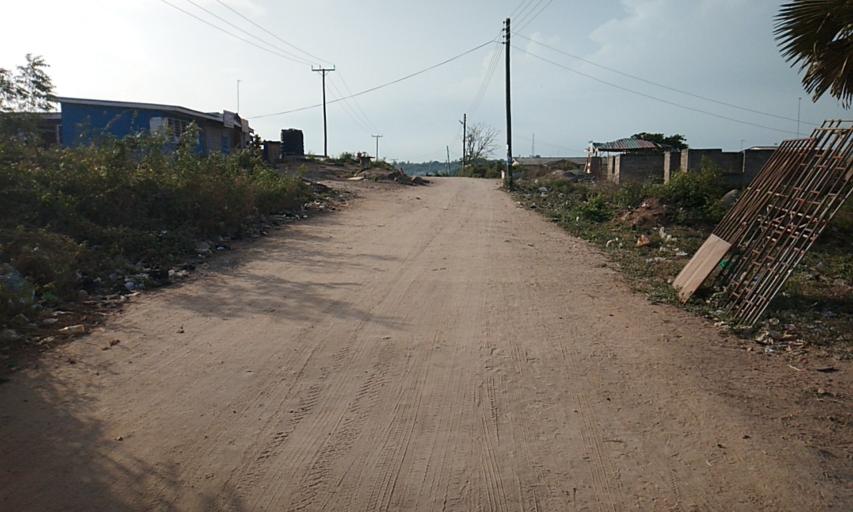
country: GH
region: Central
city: Winneba
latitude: 5.3561
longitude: -0.6135
